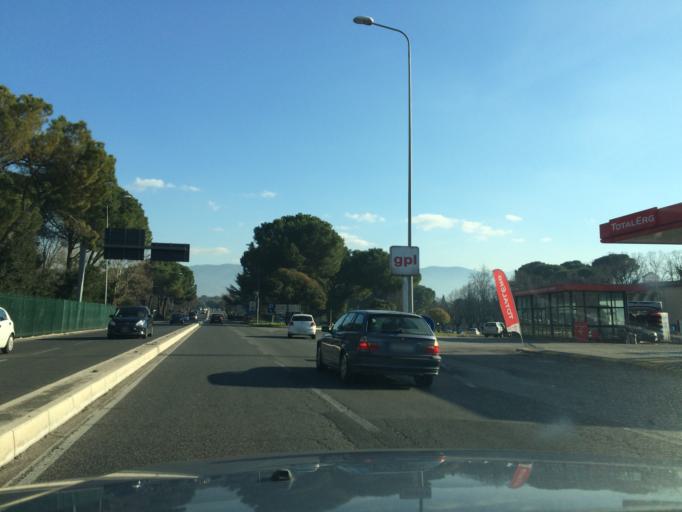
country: IT
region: Umbria
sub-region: Provincia di Terni
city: Terni
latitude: 42.5673
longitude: 12.6331
